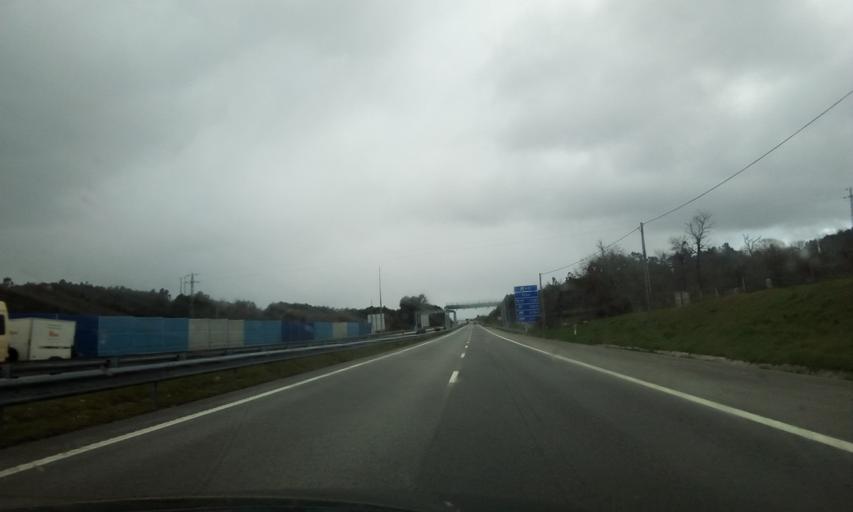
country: PT
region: Guarda
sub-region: Fornos de Algodres
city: Fornos de Algodres
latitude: 40.6134
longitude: -7.6475
